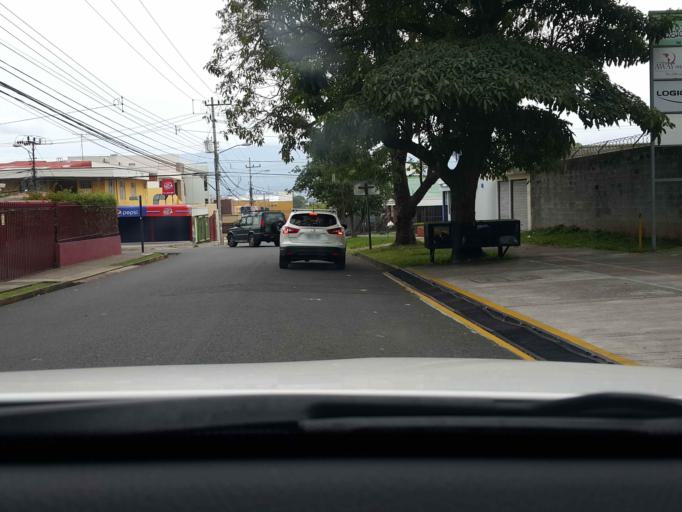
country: CR
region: San Jose
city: San Jose
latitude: 9.9391
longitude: -84.1064
